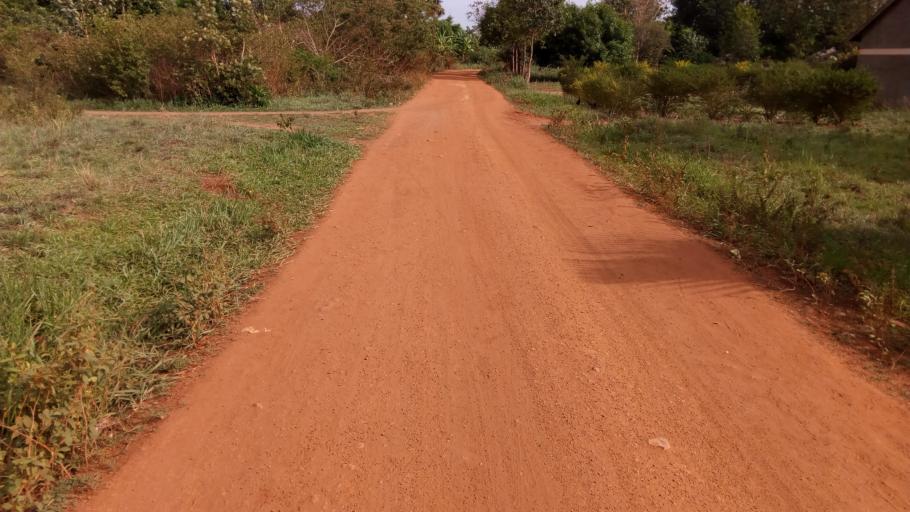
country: UG
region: Northern Region
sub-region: Gulu District
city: Gulu
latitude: 2.8012
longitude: 32.3230
